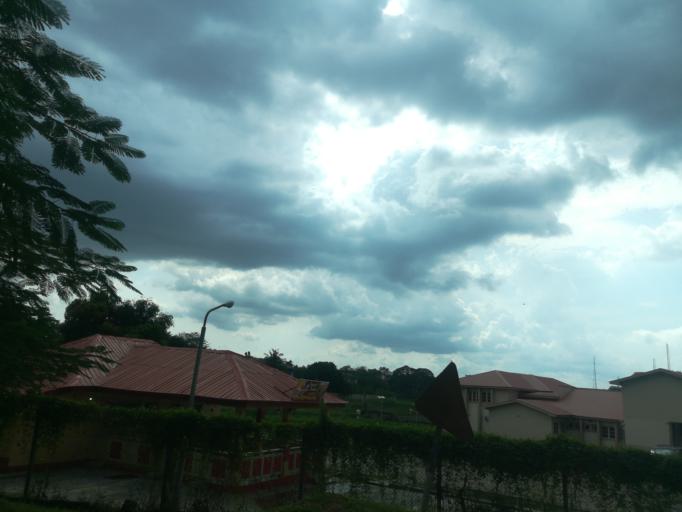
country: NG
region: Oyo
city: Ibadan
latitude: 7.4412
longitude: 3.9032
